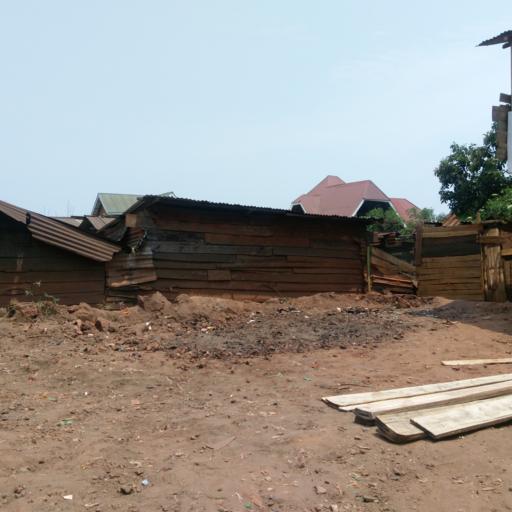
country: CD
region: Nord Kivu
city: Goma
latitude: -1.6829
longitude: 29.2429
